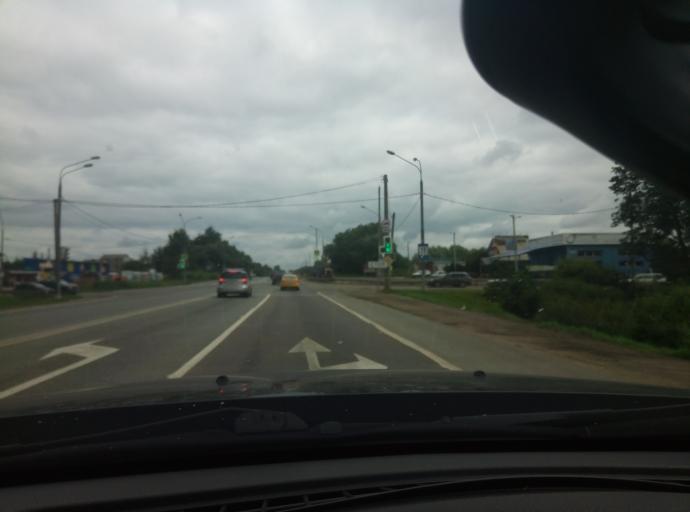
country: RU
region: Kaluga
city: Obninsk
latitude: 55.0882
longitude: 36.6336
